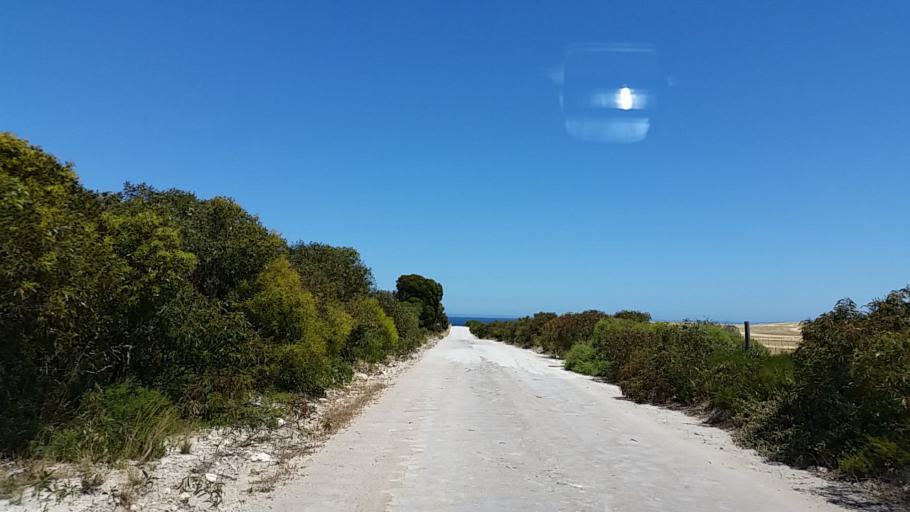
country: AU
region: South Australia
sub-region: Yorke Peninsula
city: Honiton
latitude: -35.2321
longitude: 137.1634
